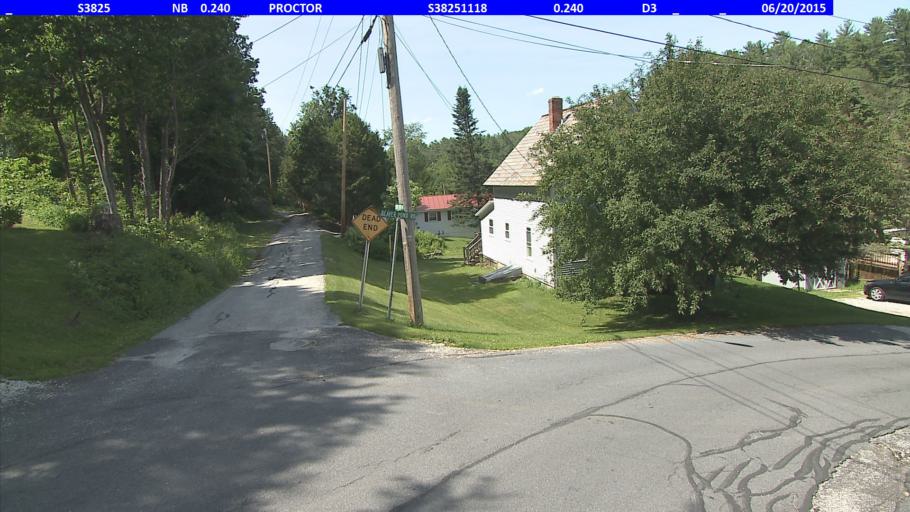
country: US
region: Vermont
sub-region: Rutland County
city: West Rutland
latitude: 43.6631
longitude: -73.0457
